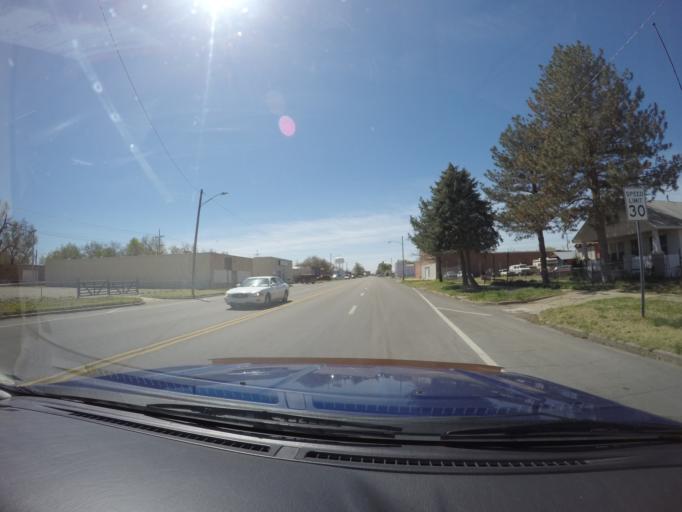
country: US
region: Kansas
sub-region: Saline County
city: Salina
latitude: 38.8560
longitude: -97.6091
